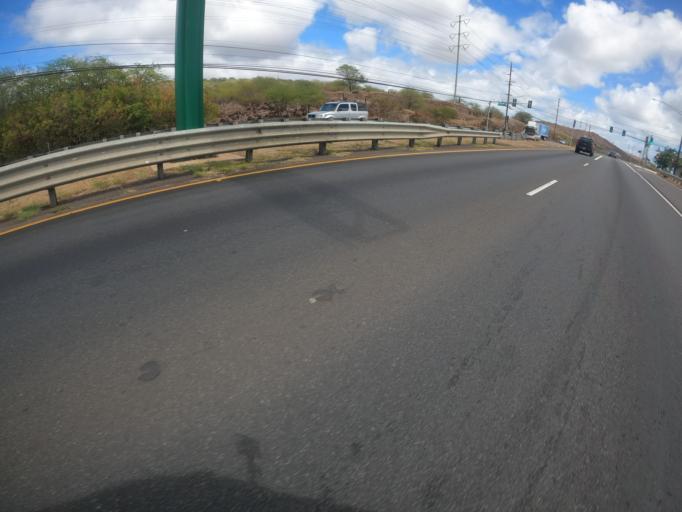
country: US
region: Hawaii
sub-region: Honolulu County
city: Makakilo City
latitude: 21.3417
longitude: -158.1070
